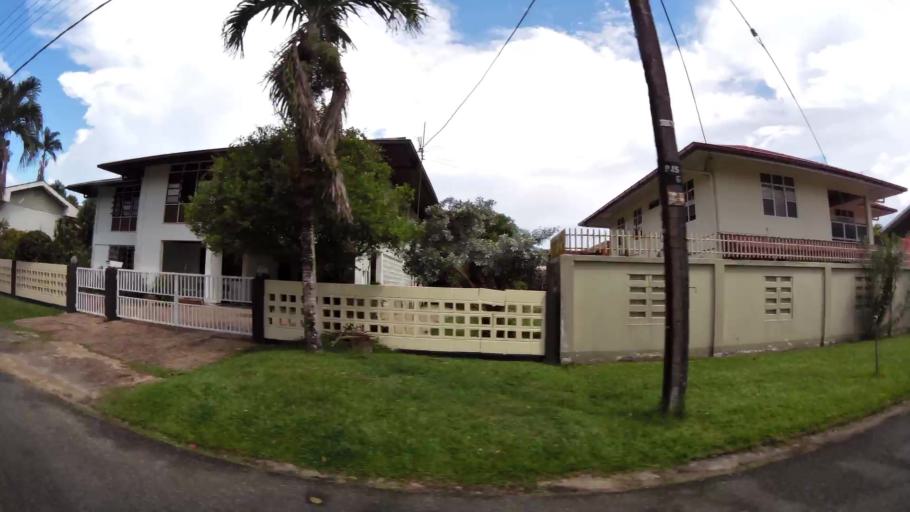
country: SR
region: Paramaribo
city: Paramaribo
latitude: 5.8360
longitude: -55.1287
